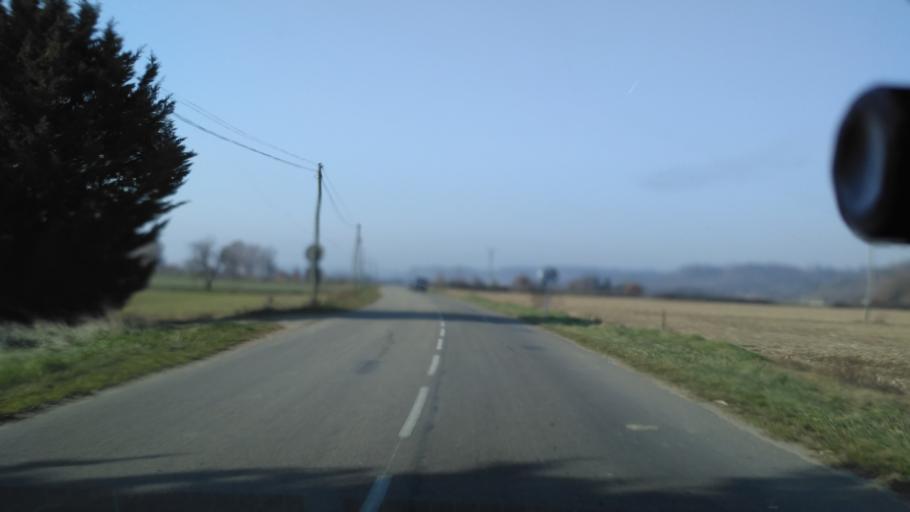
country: FR
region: Rhone-Alpes
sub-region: Departement de la Drome
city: Romans-sur-Isere
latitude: 45.0564
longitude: 5.0123
